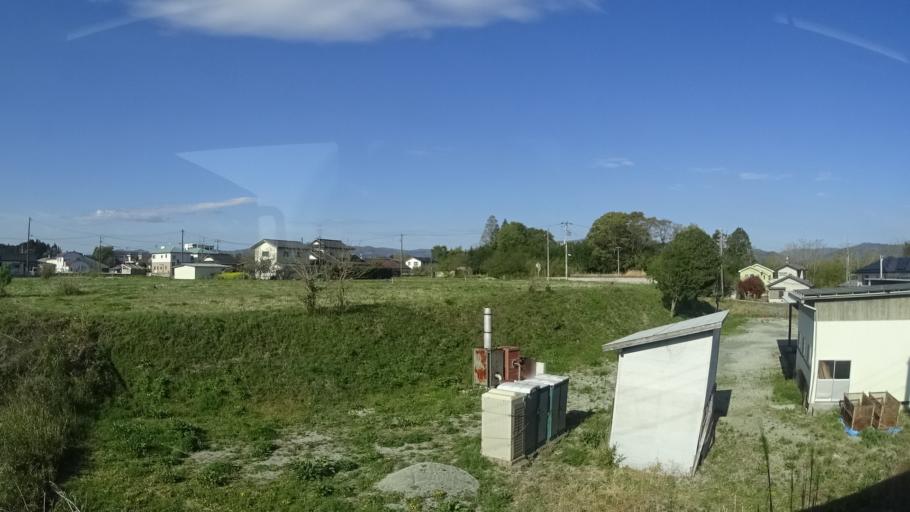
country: JP
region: Fukushima
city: Namie
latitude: 37.4974
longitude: 140.9824
